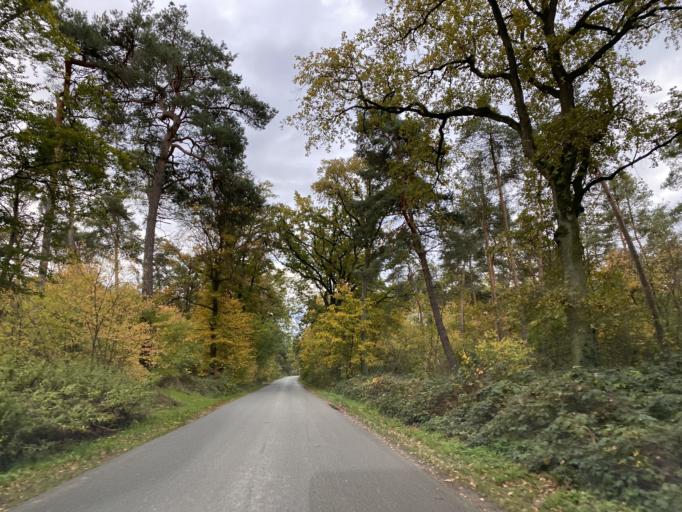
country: DE
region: Hesse
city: Griesheim
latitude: 49.8309
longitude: 8.5779
